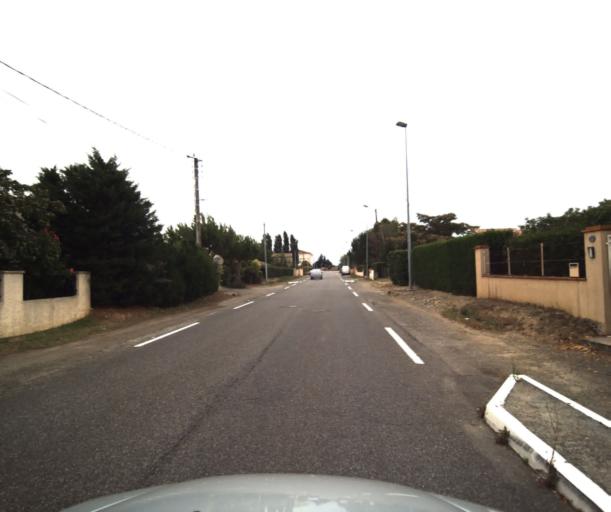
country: FR
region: Midi-Pyrenees
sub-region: Departement de la Haute-Garonne
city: Muret
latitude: 43.4517
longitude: 1.3179
